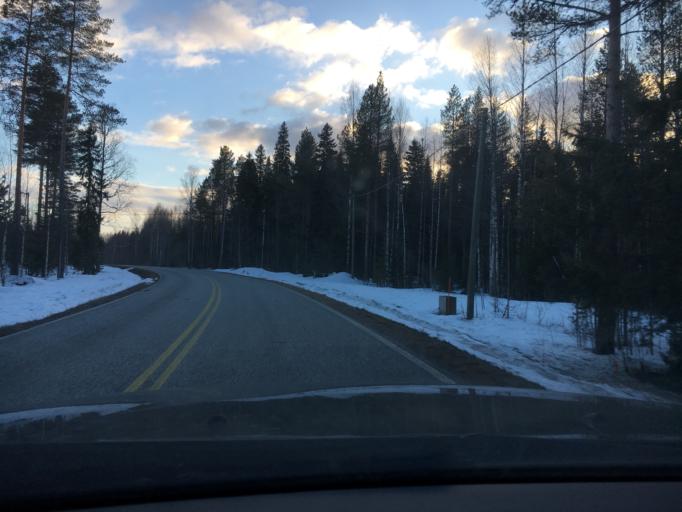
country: FI
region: Kainuu
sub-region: Kajaani
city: Kajaani
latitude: 64.2777
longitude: 27.7909
